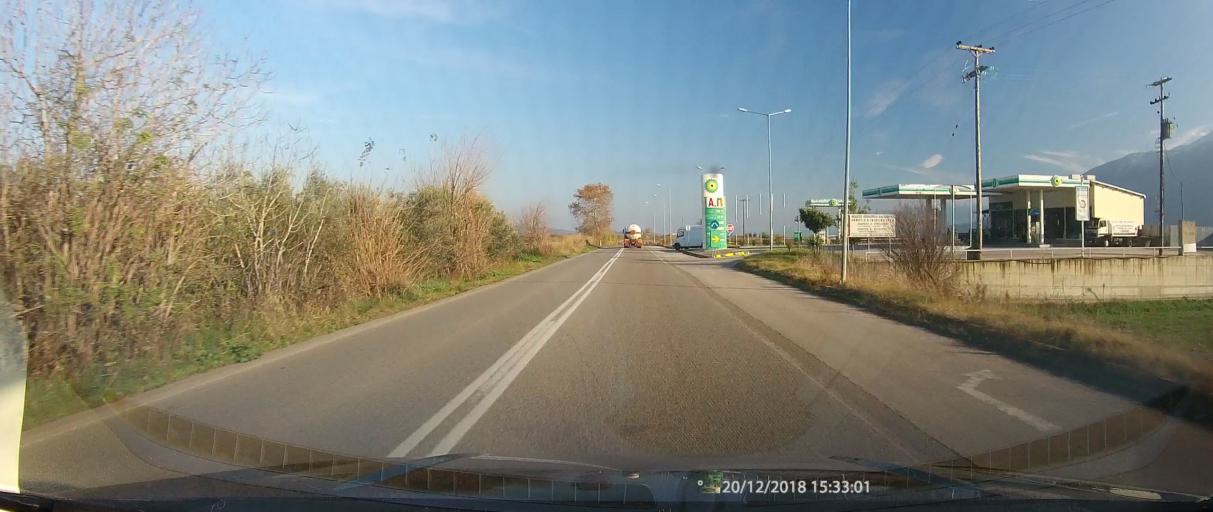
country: GR
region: Central Greece
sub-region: Nomos Fthiotidos
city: Lianokladhion
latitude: 38.9264
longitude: 22.2682
